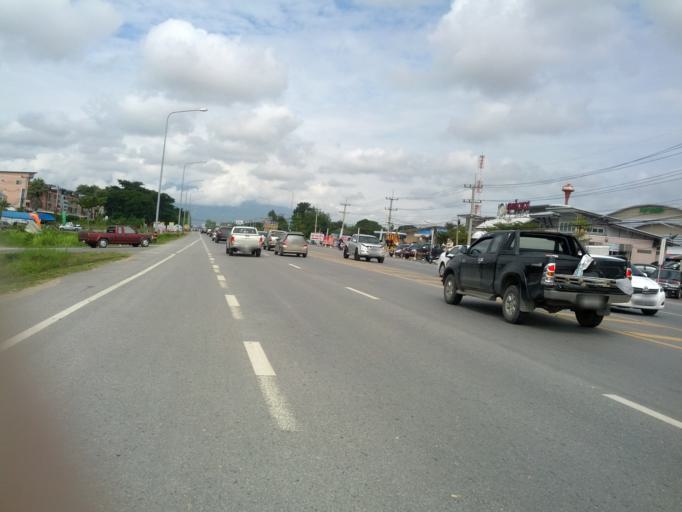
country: TH
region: Chiang Mai
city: Saraphi
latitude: 18.7536
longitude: 99.0569
